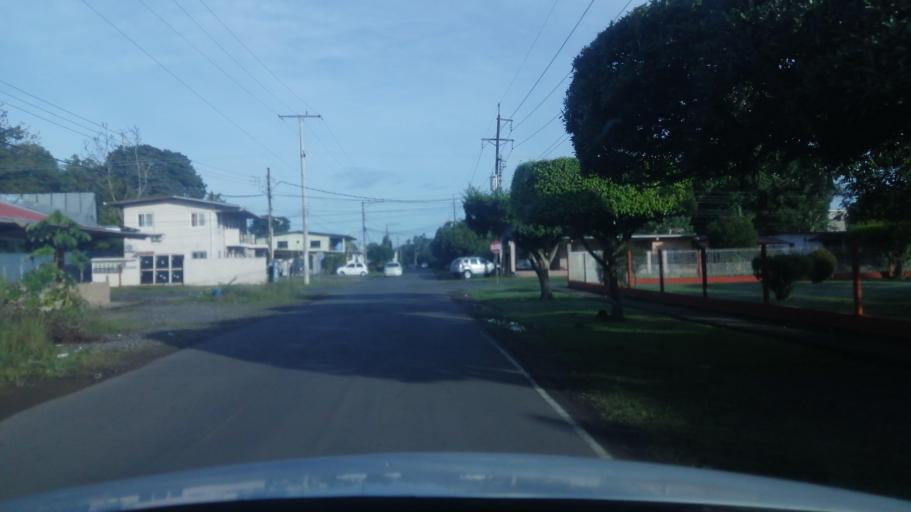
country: PA
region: Chiriqui
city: David
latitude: 8.4229
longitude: -82.4362
